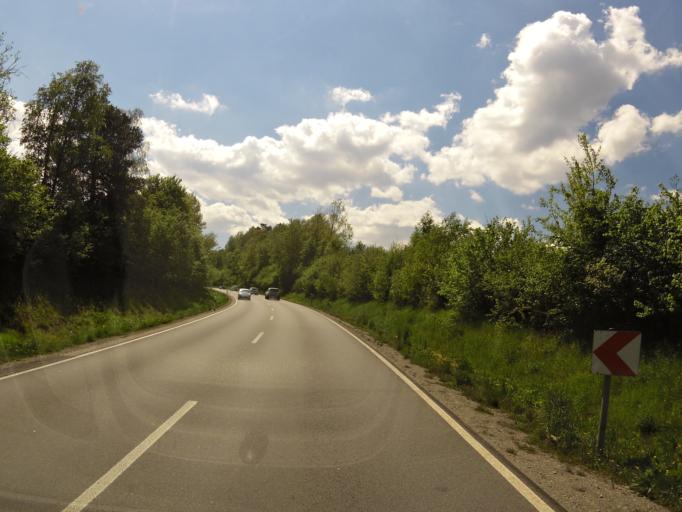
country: DE
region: Bavaria
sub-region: Lower Bavaria
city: Aicha vorm Wald
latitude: 48.6758
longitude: 13.2744
